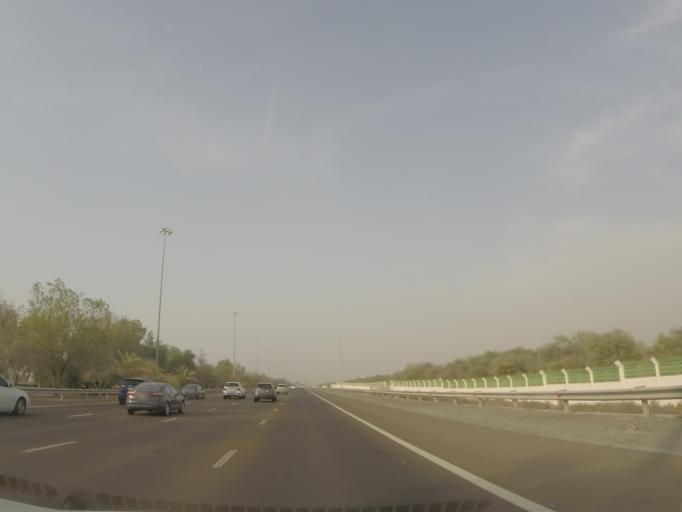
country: AE
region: Abu Dhabi
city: Abu Dhabi
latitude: 24.7172
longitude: 54.8032
